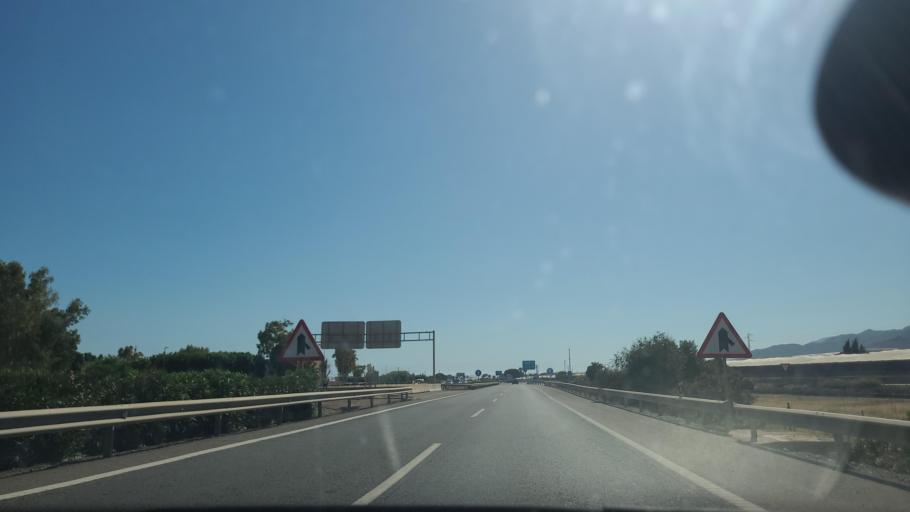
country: ES
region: Andalusia
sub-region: Provincia de Almeria
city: El Ejido
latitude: 36.7664
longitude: -2.8475
